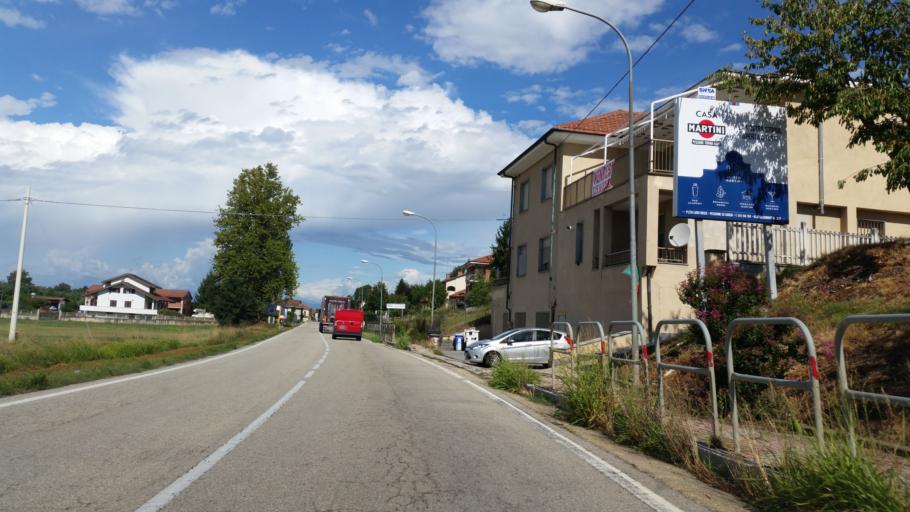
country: IT
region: Piedmont
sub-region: Provincia di Torino
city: Pralormo
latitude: 44.8573
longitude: 7.9048
